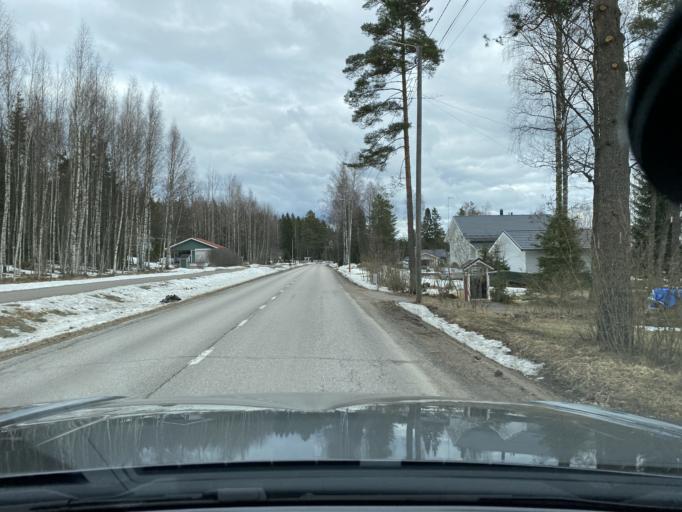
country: FI
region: Uusimaa
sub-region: Helsinki
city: Hyvinge
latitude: 60.5825
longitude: 24.7919
